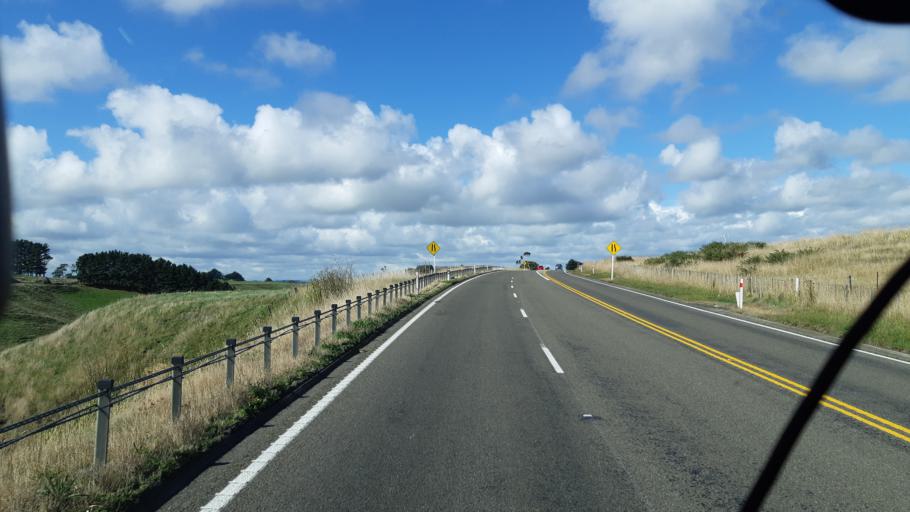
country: NZ
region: Manawatu-Wanganui
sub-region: Wanganui District
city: Wanganui
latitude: -40.0259
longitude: 175.1892
